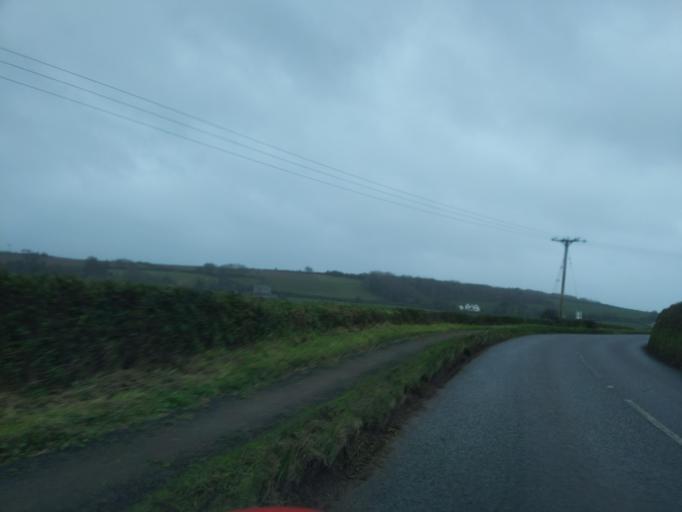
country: GB
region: England
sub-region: Cornwall
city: Saltash
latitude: 50.3651
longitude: -4.2605
